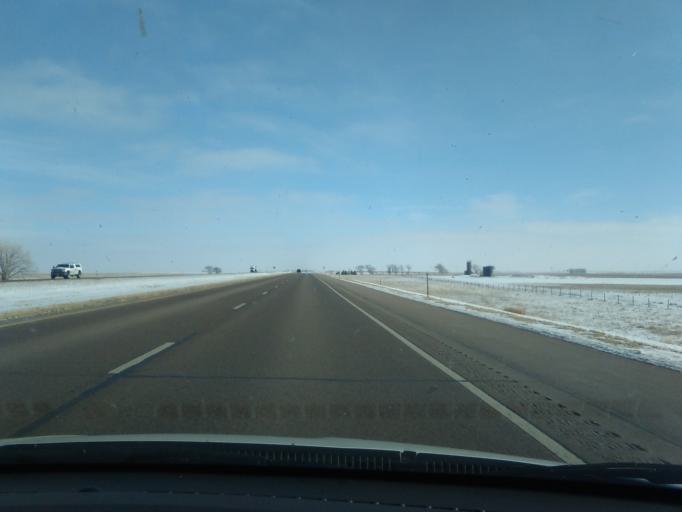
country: US
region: Nebraska
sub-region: Kimball County
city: Kimball
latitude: 41.1919
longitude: -103.8307
